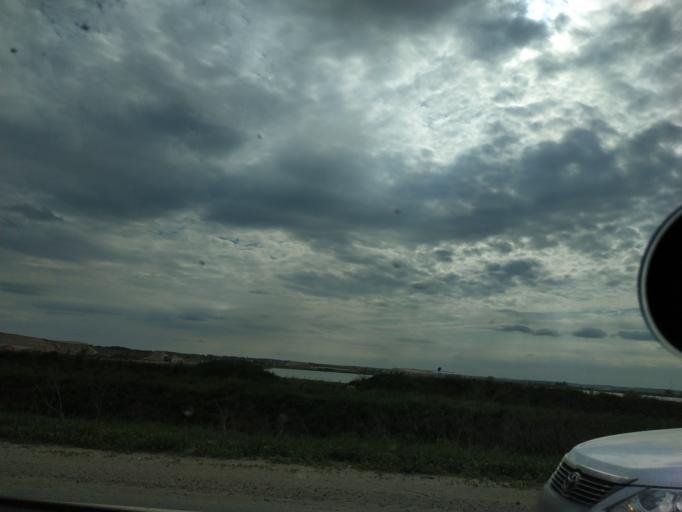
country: RU
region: Moskovskaya
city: Malyshevo
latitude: 55.5077
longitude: 38.2873
